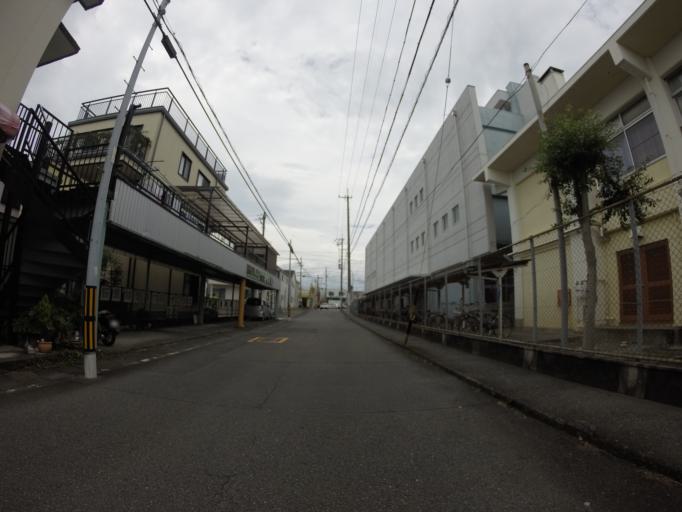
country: JP
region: Shizuoka
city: Shizuoka-shi
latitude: 34.9627
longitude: 138.4099
